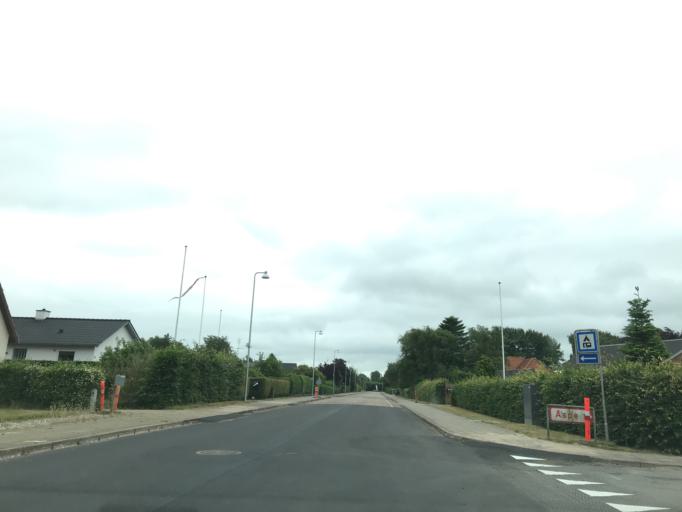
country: DK
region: South Denmark
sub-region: Tonder Kommune
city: Sherrebek
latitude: 55.0542
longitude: 8.8284
